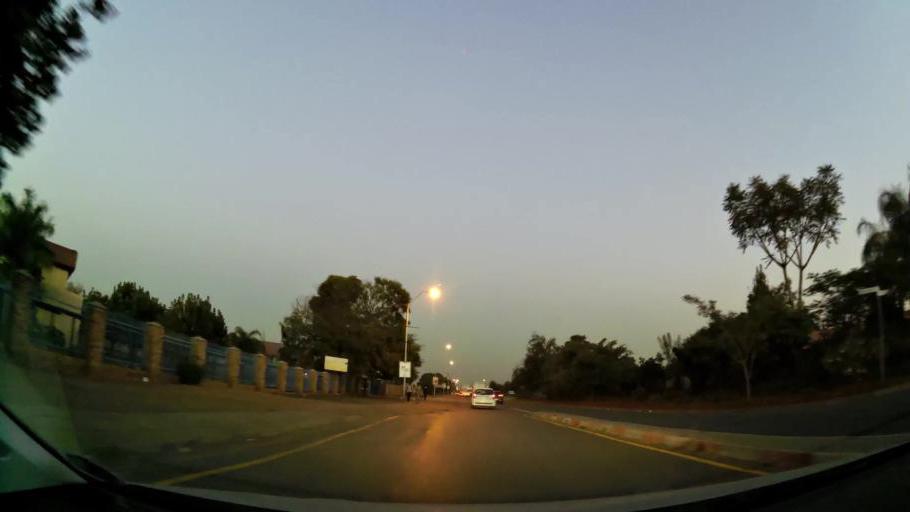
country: ZA
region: North-West
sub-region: Bojanala Platinum District Municipality
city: Rustenburg
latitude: -25.6763
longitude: 27.2491
